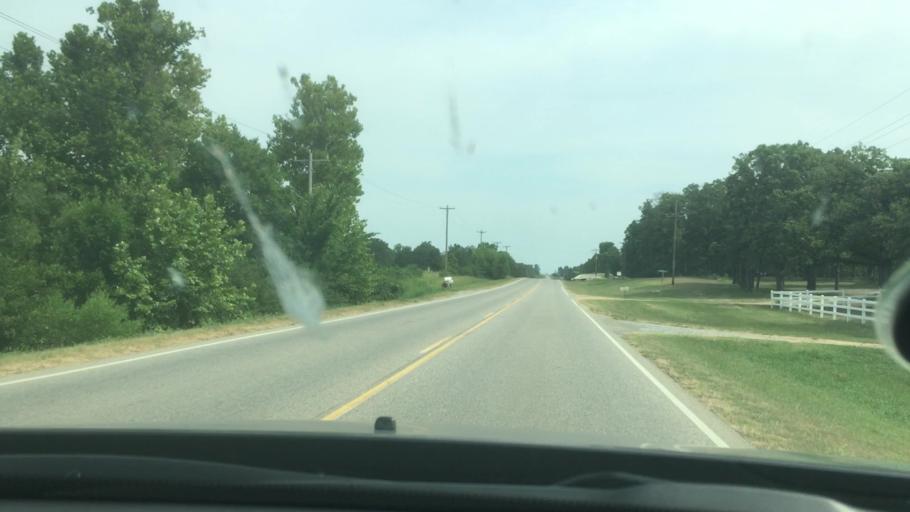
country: US
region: Oklahoma
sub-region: Johnston County
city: Tishomingo
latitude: 34.2558
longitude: -96.4248
